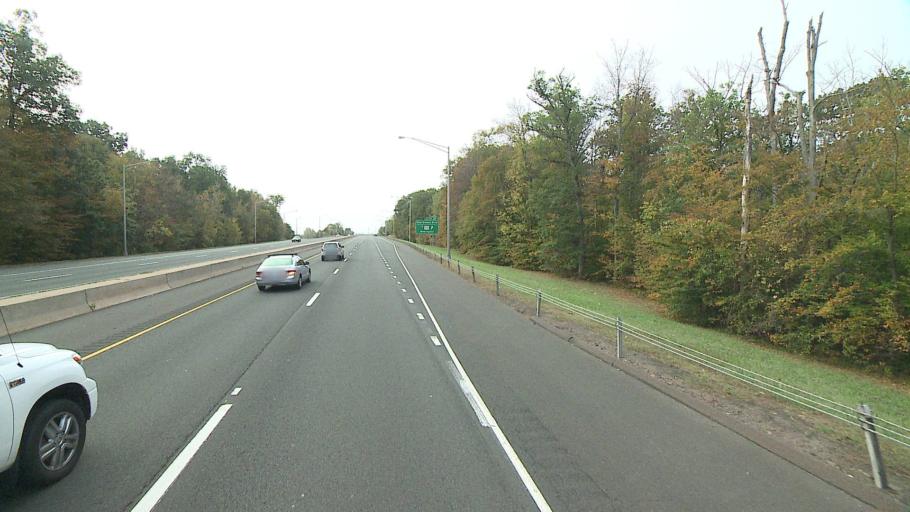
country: US
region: Connecticut
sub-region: Hartford County
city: Newington
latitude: 41.7044
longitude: -72.7578
